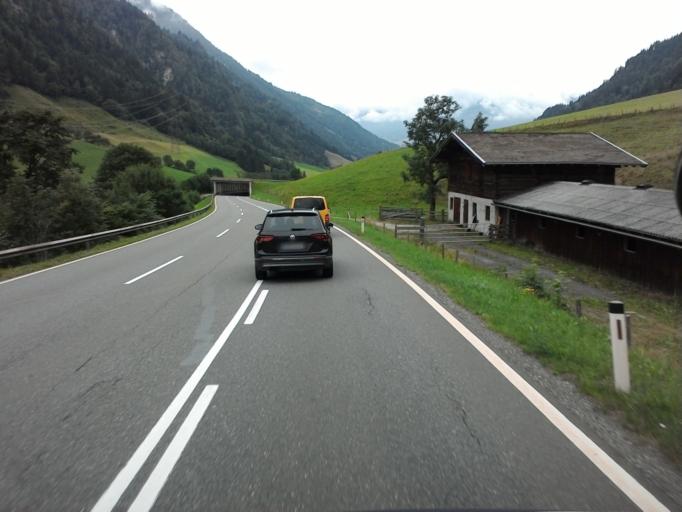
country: AT
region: Salzburg
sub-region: Politischer Bezirk Zell am See
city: Mittersill
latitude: 47.2358
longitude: 12.4938
